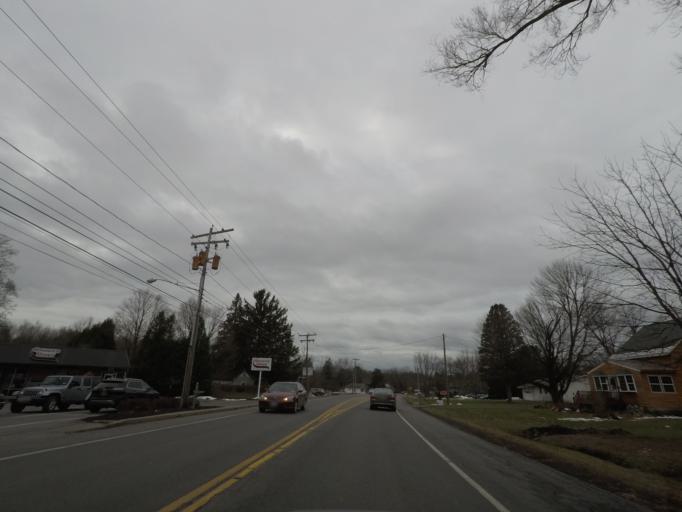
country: US
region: New York
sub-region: Schenectady County
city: East Glenville
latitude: 42.9011
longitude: -73.9059
